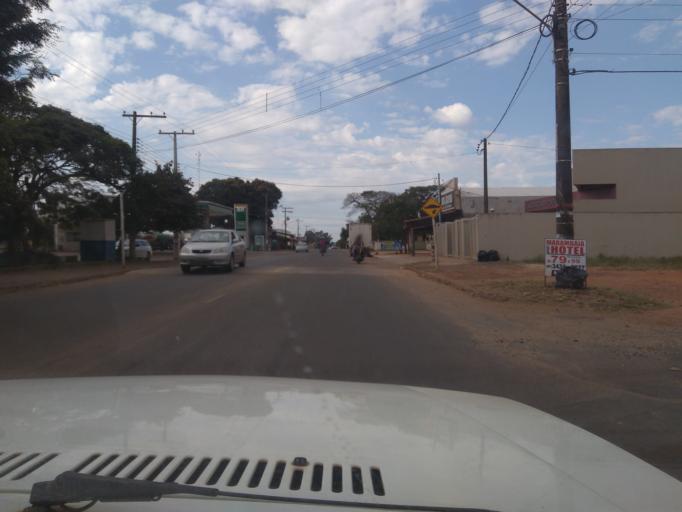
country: BR
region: Mato Grosso do Sul
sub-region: Ponta Pora
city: Ponta Pora
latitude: -22.5620
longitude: -55.6947
